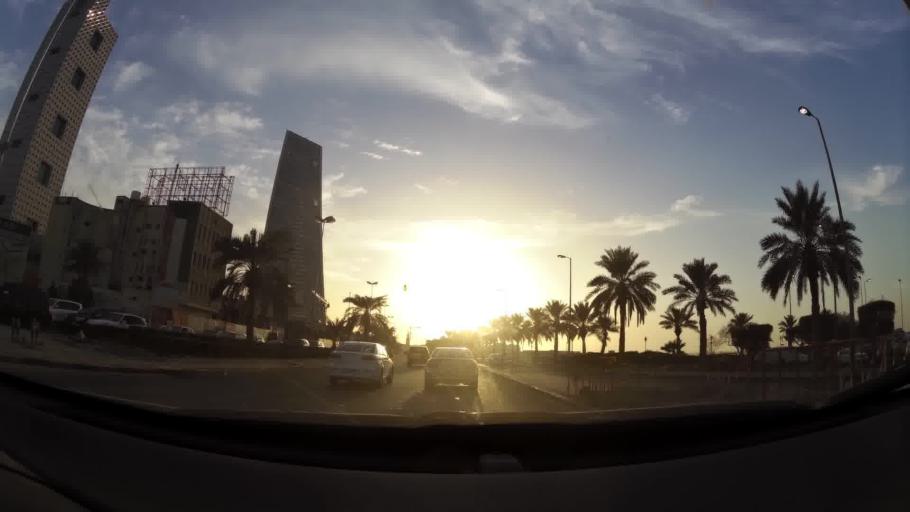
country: KW
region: Al Asimah
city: Kuwait City
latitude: 29.3858
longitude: 47.9799
